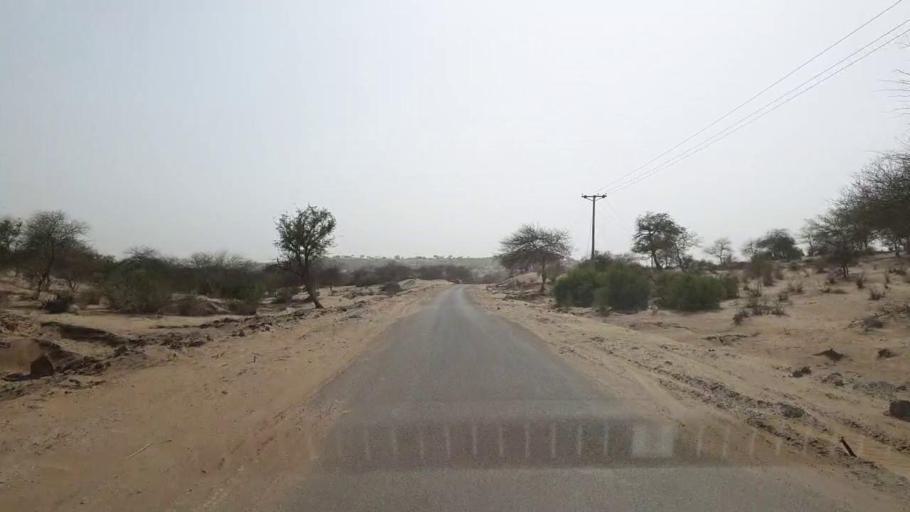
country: PK
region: Sindh
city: Mithi
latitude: 24.6187
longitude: 69.8884
